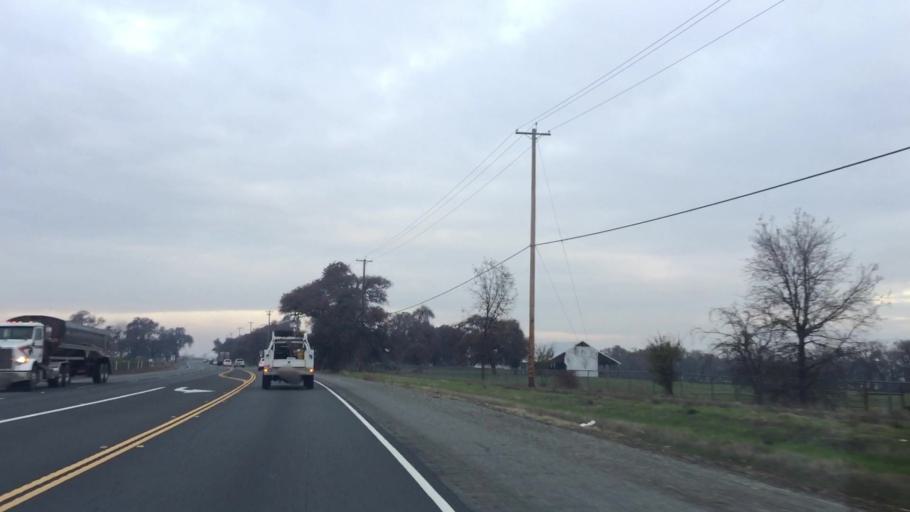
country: US
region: California
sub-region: Butte County
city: Gridley
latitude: 39.3510
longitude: -121.6016
